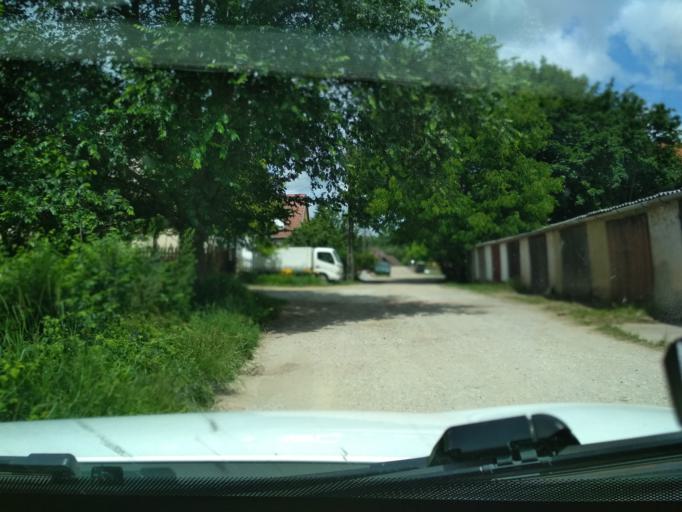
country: HU
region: Jasz-Nagykun-Szolnok
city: Tiszafured
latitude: 47.6198
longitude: 20.7445
